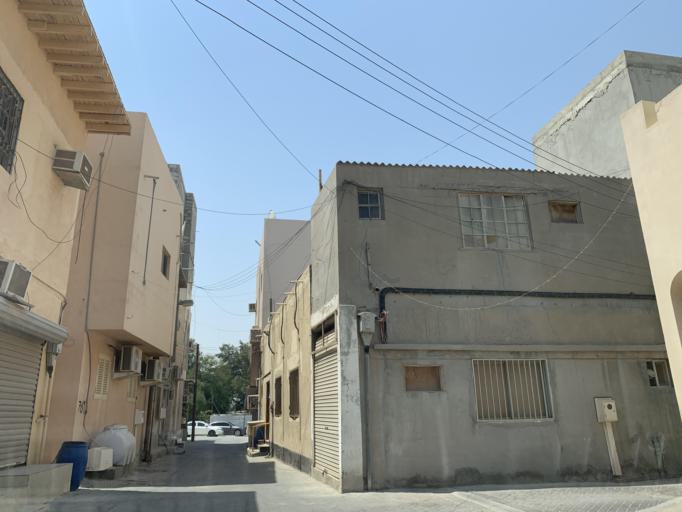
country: BH
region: Manama
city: Jidd Hafs
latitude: 26.2029
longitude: 50.5198
